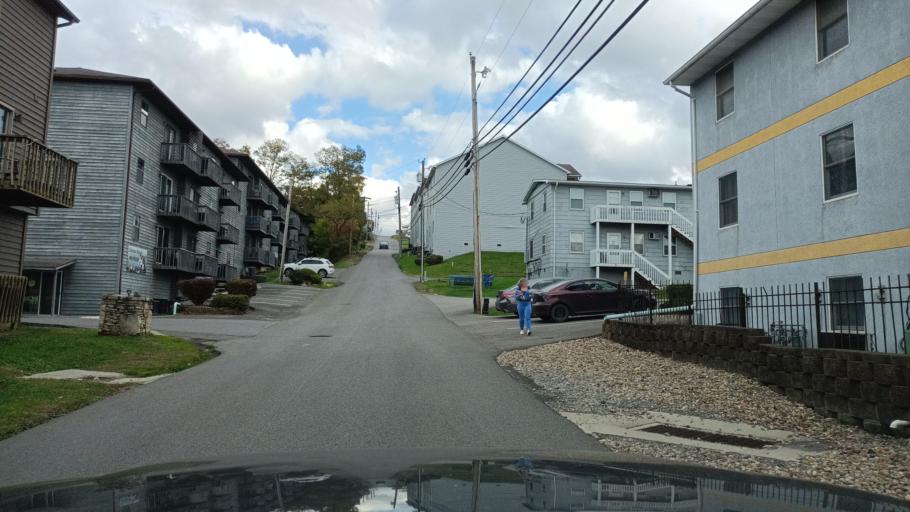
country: US
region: West Virginia
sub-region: Monongalia County
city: Morgantown
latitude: 39.6509
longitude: -79.9503
